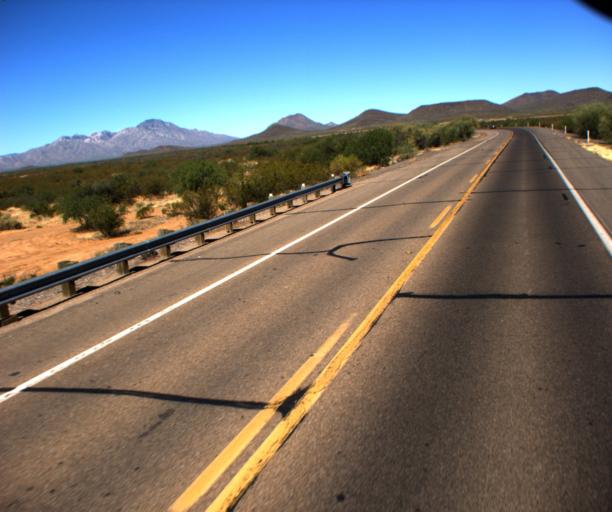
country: US
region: Arizona
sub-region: Pima County
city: Three Points
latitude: 32.0758
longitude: -111.3397
